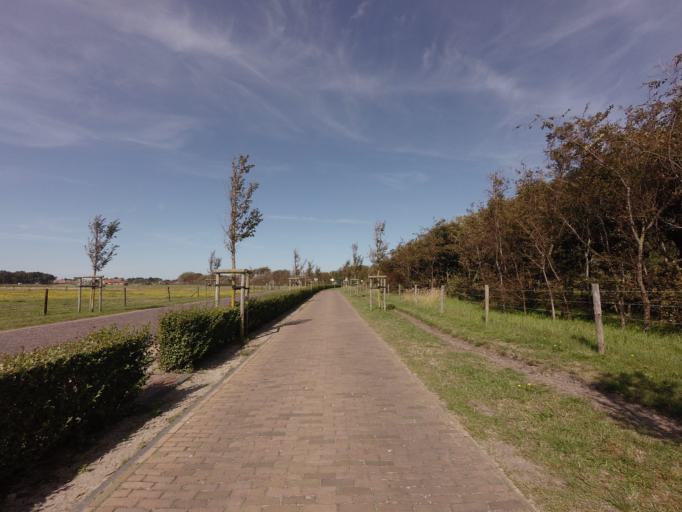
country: NL
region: Friesland
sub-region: Gemeente Ameland
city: Hollum
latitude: 53.4450
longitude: 5.6351
